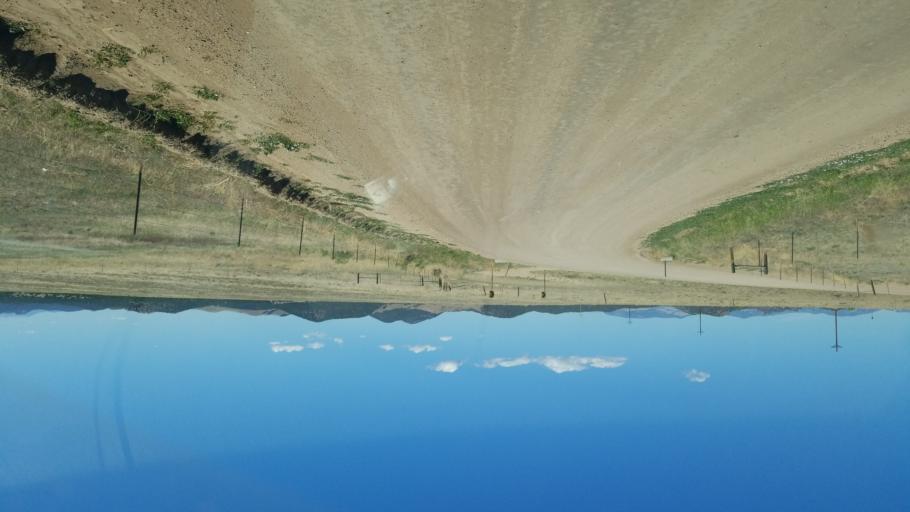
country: US
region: Colorado
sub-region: Custer County
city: Westcliffe
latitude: 38.2618
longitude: -105.5000
